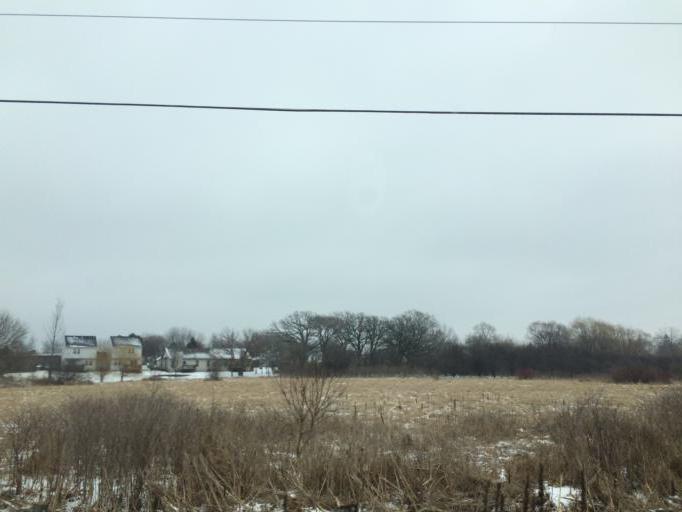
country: US
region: Illinois
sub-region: McHenry County
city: Woodstock
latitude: 42.2865
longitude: -88.4331
